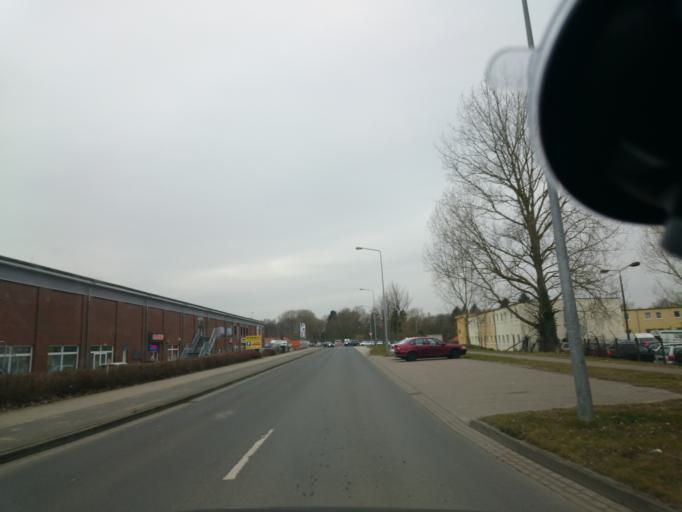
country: DE
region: Mecklenburg-Vorpommern
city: Bad Doberan
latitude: 54.1094
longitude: 11.9212
